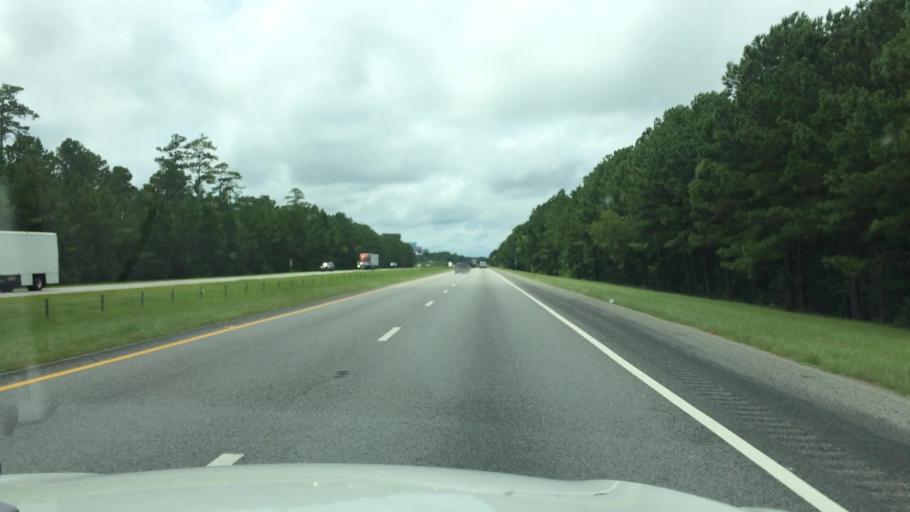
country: US
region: South Carolina
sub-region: Florence County
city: Timmonsville
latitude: 34.2072
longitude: -79.9341
